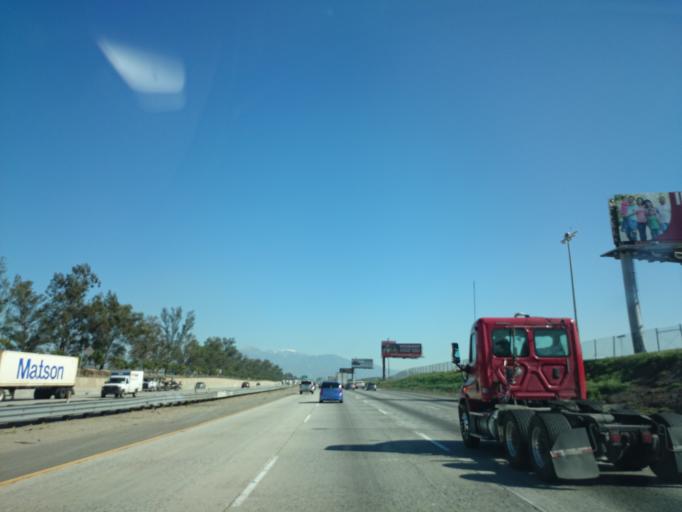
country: US
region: California
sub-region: San Bernardino County
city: Bloomington
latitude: 34.0682
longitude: -117.3890
